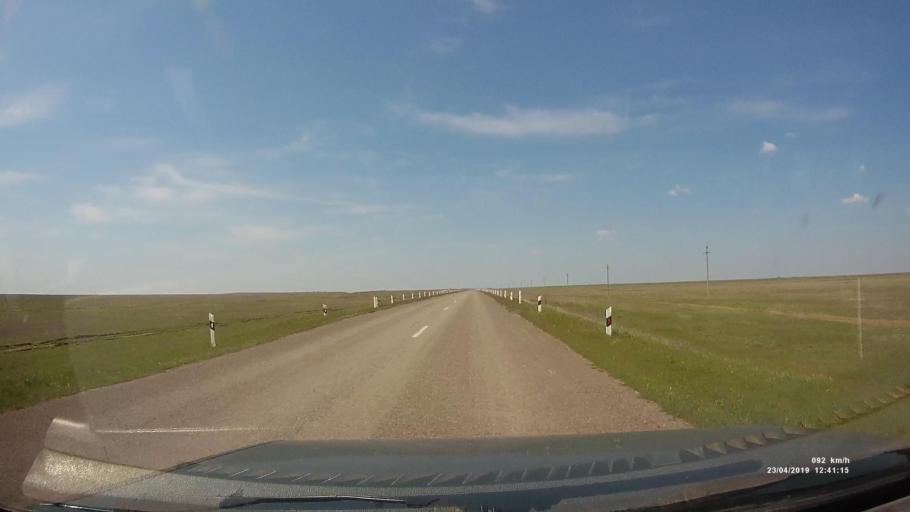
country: RU
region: Kalmykiya
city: Yashalta
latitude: 46.4467
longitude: 42.6838
